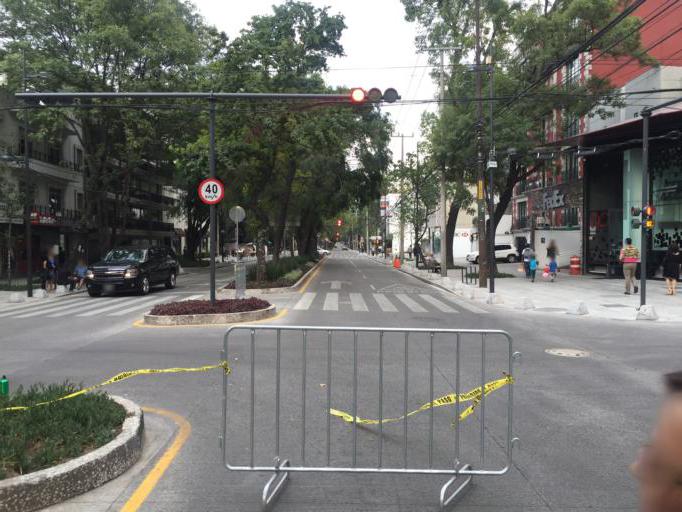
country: MX
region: Mexico City
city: Miguel Hidalgo
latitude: 19.4314
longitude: -99.1882
